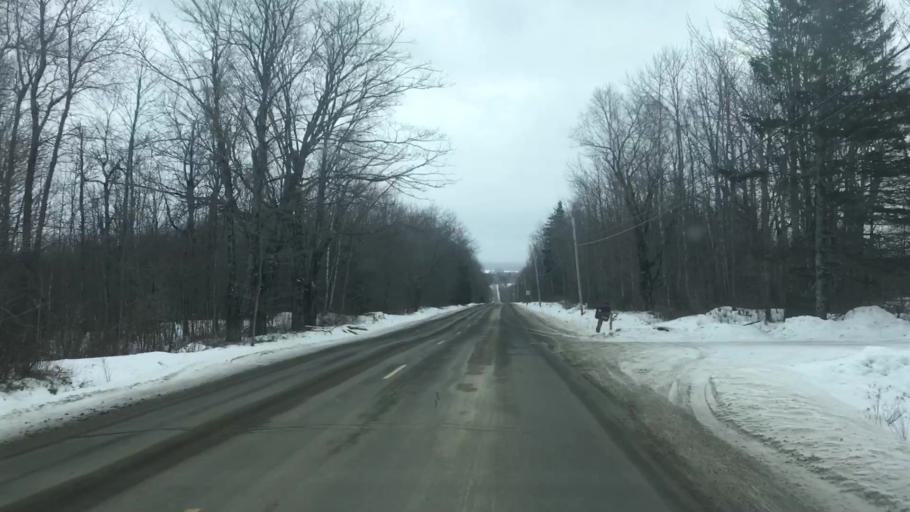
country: US
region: Maine
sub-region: Washington County
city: East Machias
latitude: 44.9768
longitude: -67.4515
